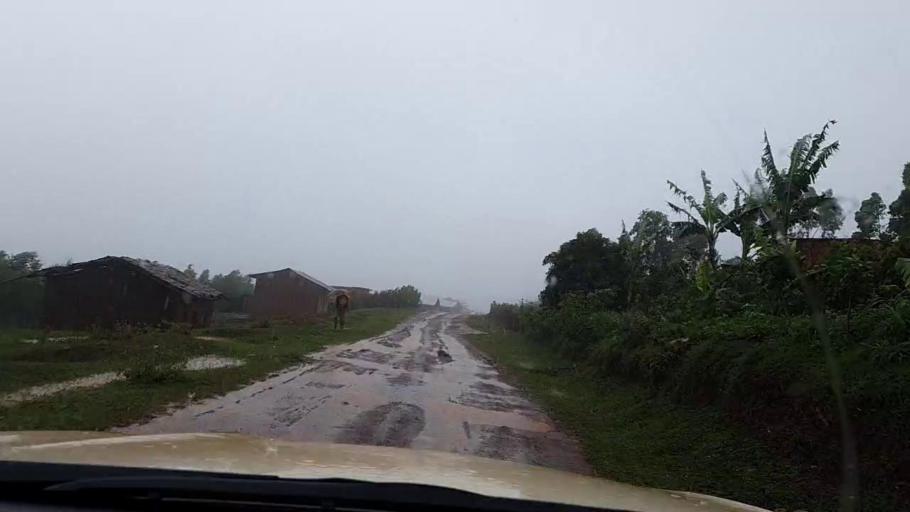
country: RW
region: Northern Province
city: Byumba
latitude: -1.7350
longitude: 30.0123
